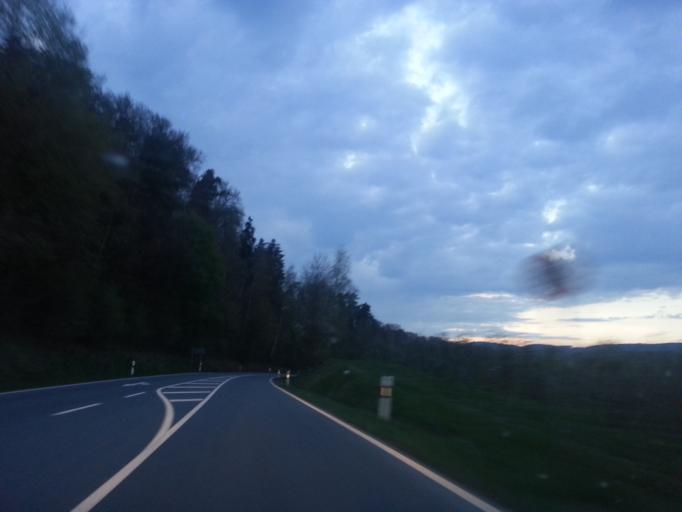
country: DE
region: Baden-Wuerttemberg
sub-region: Tuebingen Region
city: Oberteuringen
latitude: 47.6904
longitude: 9.4407
